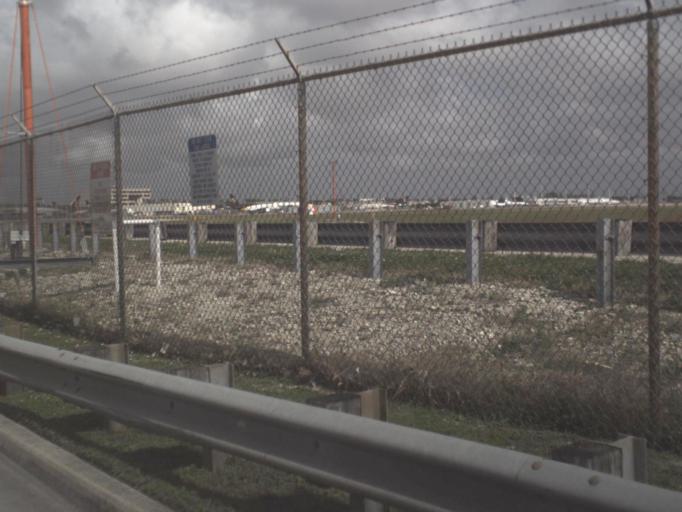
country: US
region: Florida
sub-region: Miami-Dade County
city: Virginia Gardens
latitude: 25.8004
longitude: -80.3064
